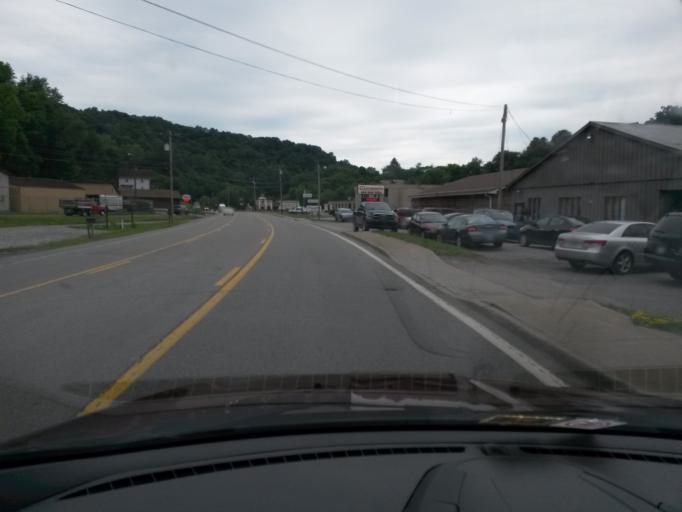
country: US
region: West Virginia
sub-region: Lewis County
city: Weston
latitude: 39.0369
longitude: -80.4513
